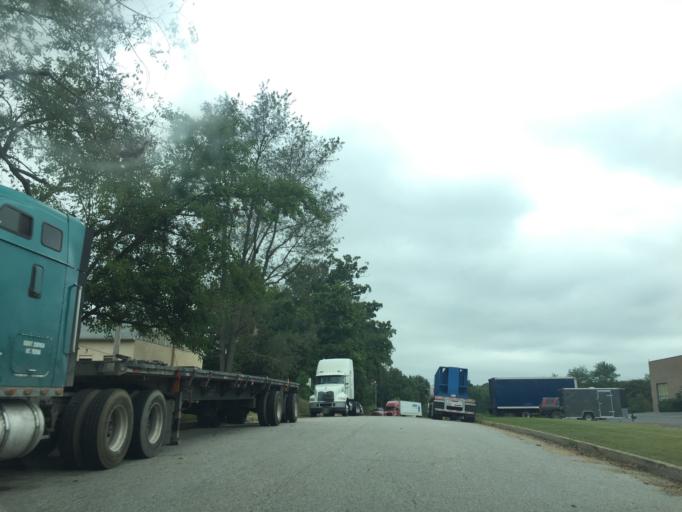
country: US
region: Maryland
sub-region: Harford County
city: Bel Air North
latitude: 39.5668
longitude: -76.3635
